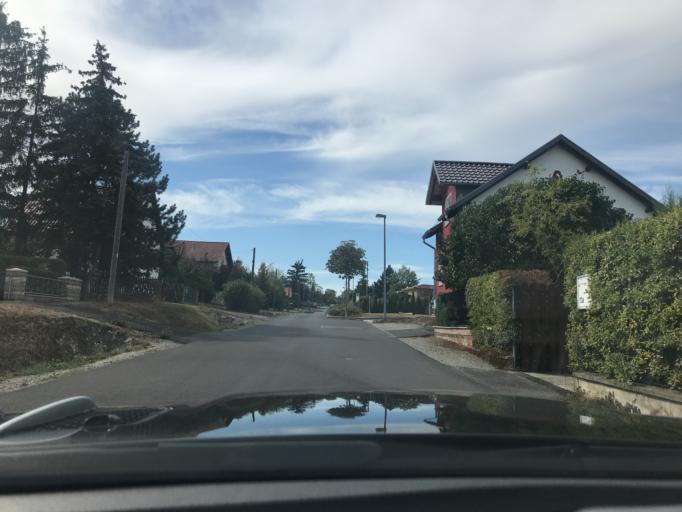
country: DE
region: Thuringia
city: Muehlhausen
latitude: 51.2140
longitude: 10.4403
